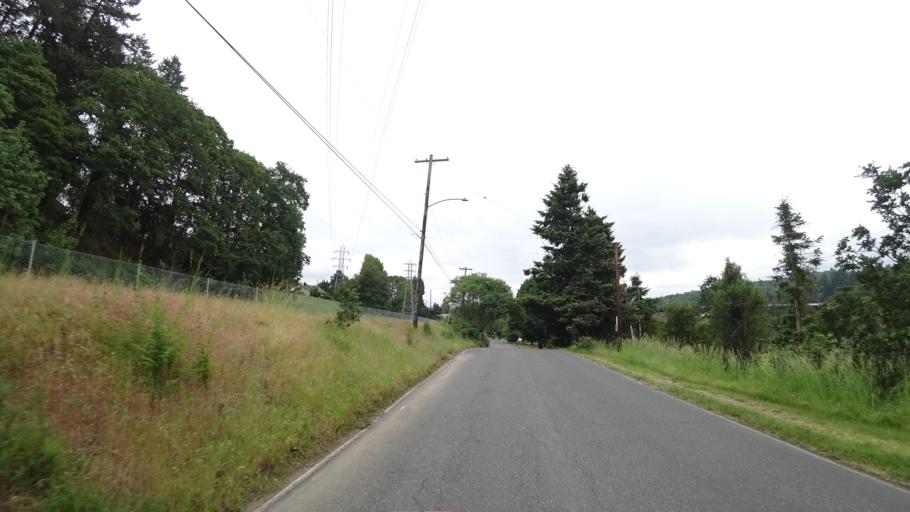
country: US
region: Oregon
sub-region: Clackamas County
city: Milwaukie
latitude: 45.4671
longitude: -122.6625
